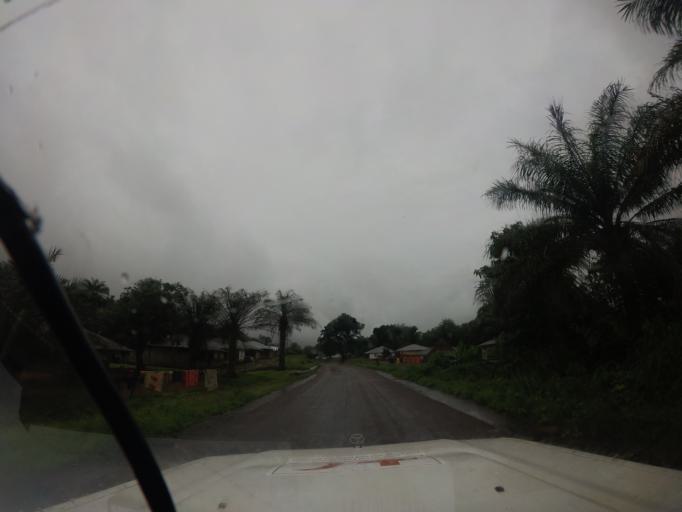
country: SL
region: Northern Province
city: Bumbuna
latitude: 9.3060
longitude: -11.9447
